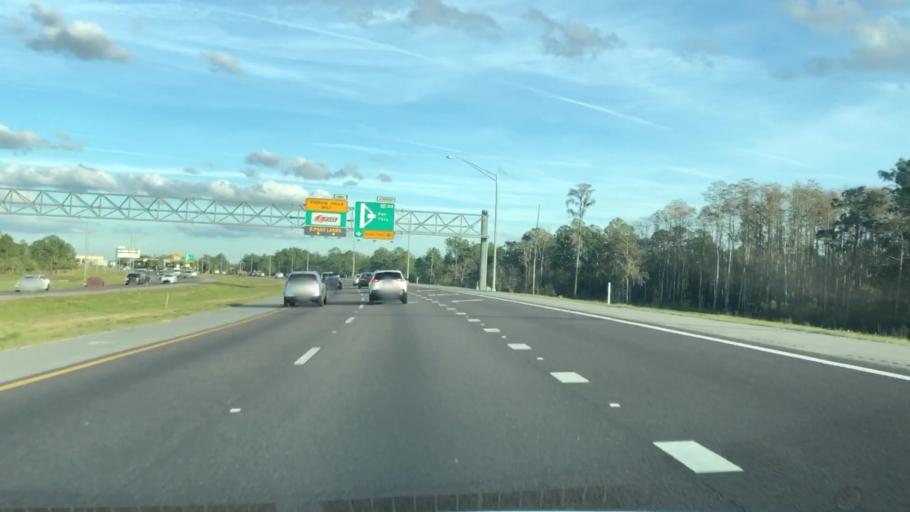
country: US
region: Florida
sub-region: Orange County
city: Hunters Creek
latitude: 28.3539
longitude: -81.4687
